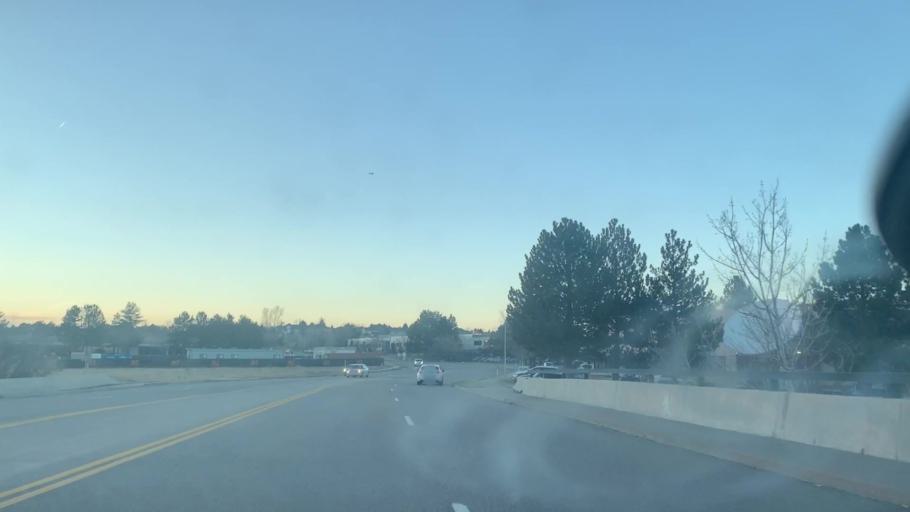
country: US
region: Colorado
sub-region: Arapahoe County
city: Centennial
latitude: 39.5974
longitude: -104.8581
